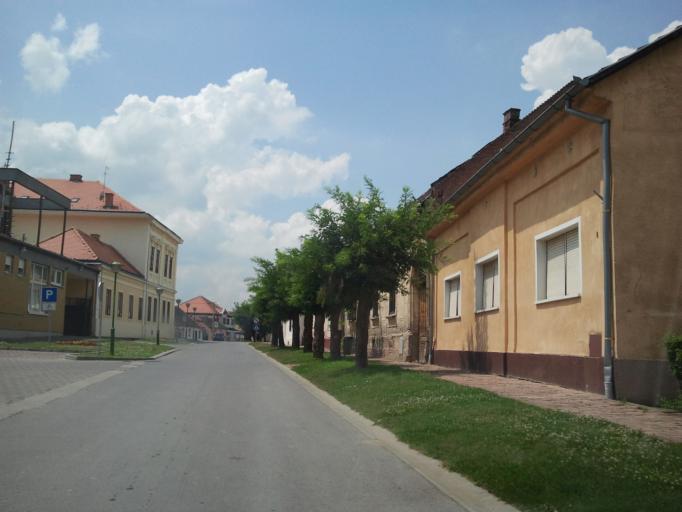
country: HR
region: Vukovarsko-Srijemska
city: Ilok
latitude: 45.2237
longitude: 19.3713
